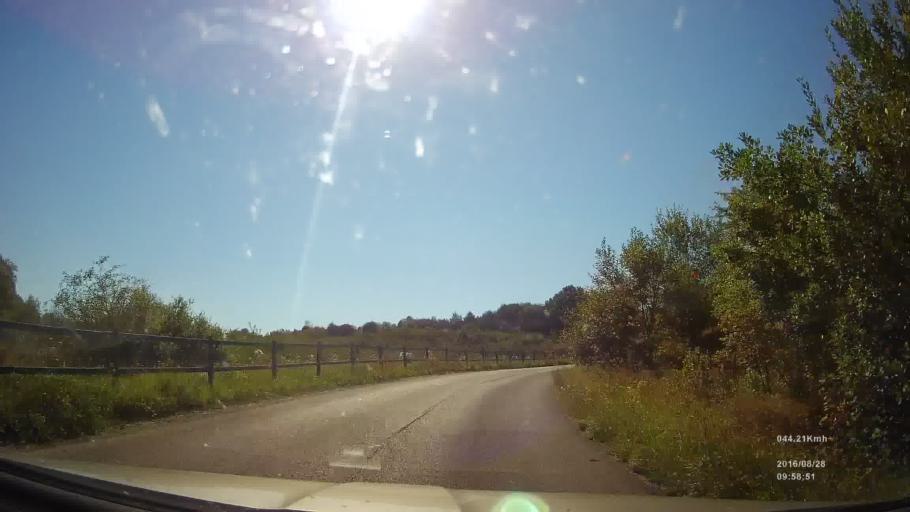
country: SK
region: Zilinsky
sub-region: Okres Liptovsky Mikulas
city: Liptovsky Mikulas
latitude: 49.1149
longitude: 19.4795
